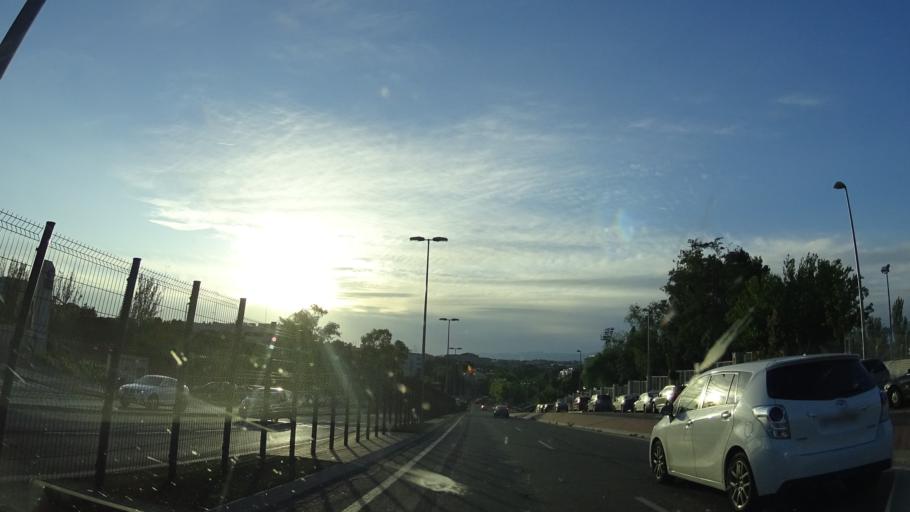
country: ES
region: Madrid
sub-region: Provincia de Madrid
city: San Sebastian de los Reyes
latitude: 40.5350
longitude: -3.6210
